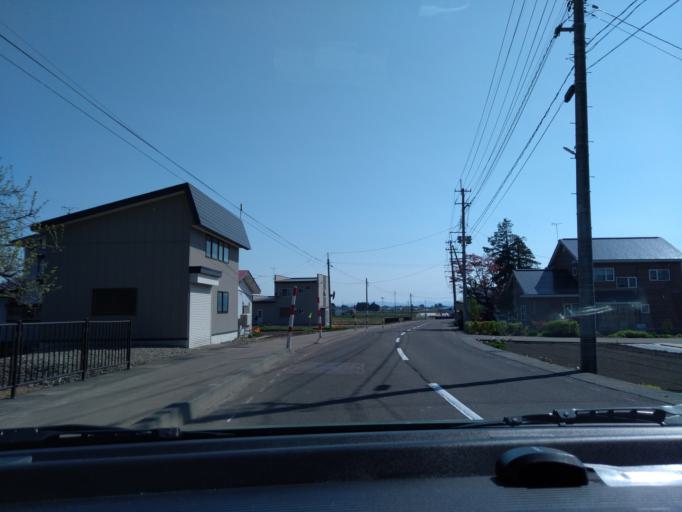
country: JP
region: Akita
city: Omagari
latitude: 39.4537
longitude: 140.5772
